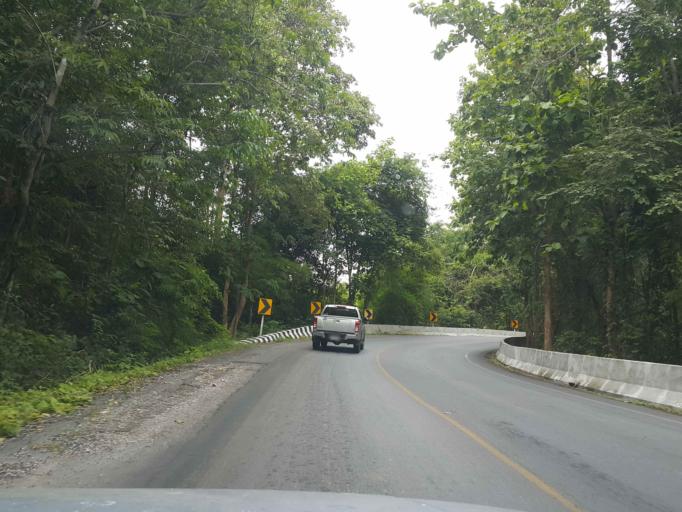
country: TH
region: Lampang
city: Thoen
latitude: 17.6137
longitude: 99.3240
